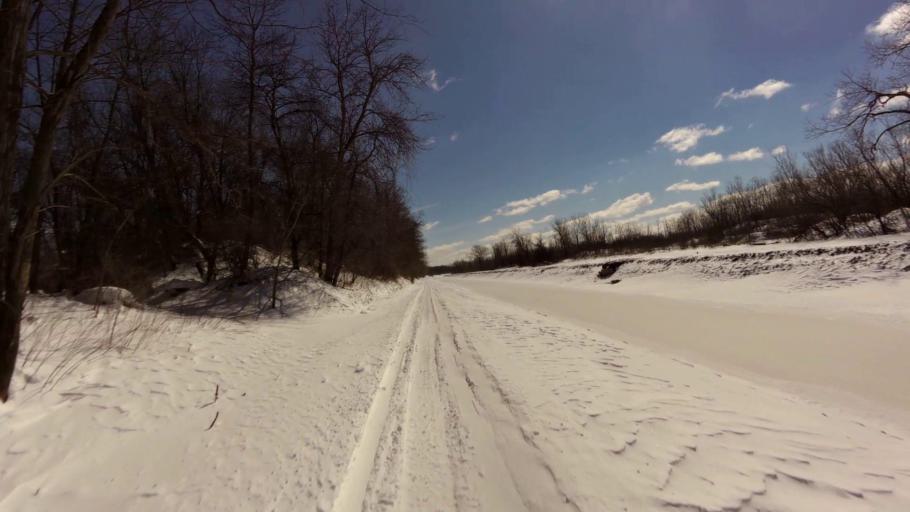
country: US
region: New York
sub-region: Orleans County
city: Holley
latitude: 43.2540
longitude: -78.0582
